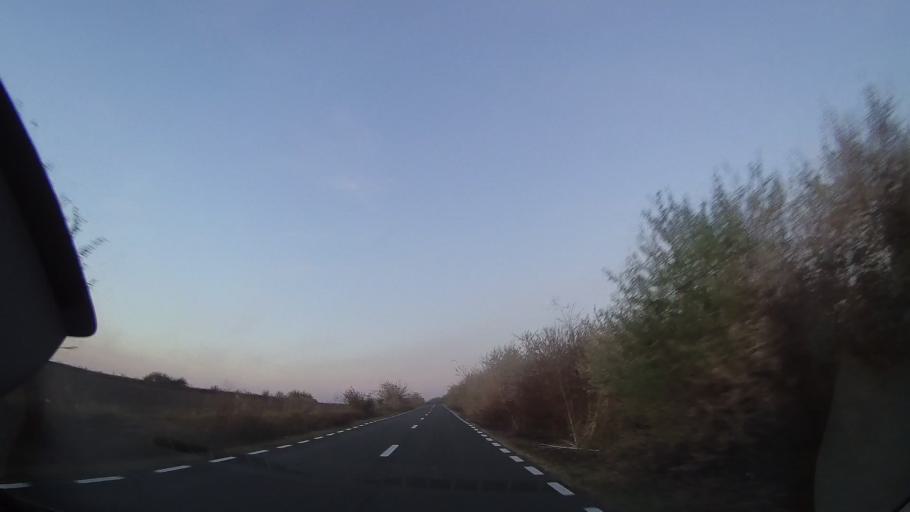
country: RO
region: Constanta
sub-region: Comuna Cobadin
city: Cobadin
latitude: 44.0328
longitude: 28.2606
